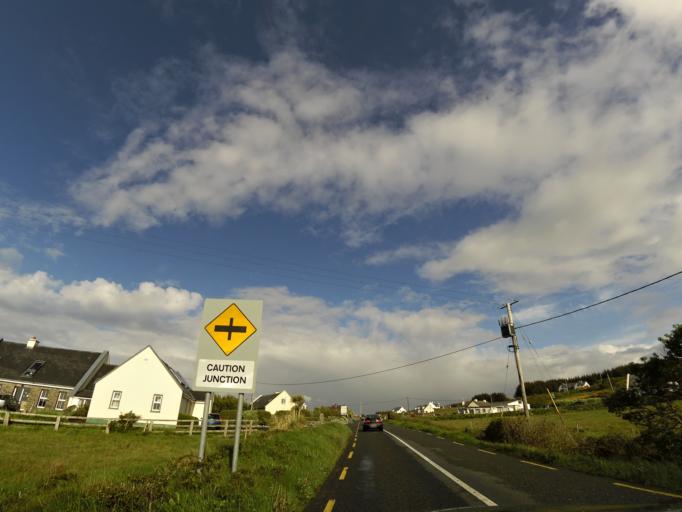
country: IE
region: Connaught
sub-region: County Galway
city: Bearna
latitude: 53.0082
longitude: -9.3556
